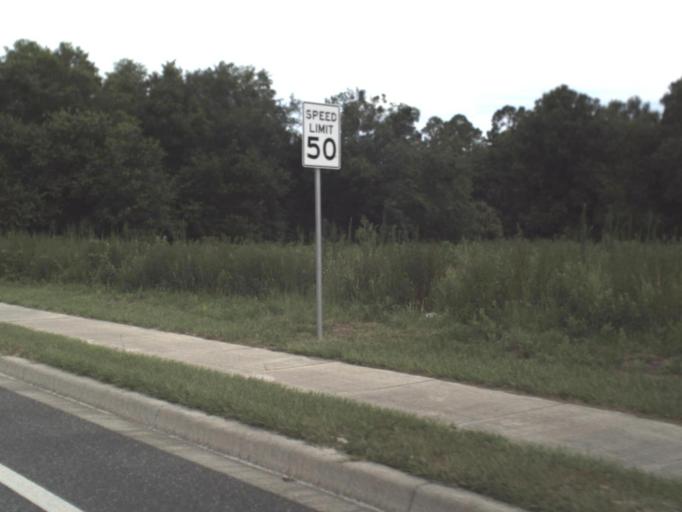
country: US
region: Florida
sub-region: Putnam County
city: Palatka
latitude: 29.6299
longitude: -81.7253
